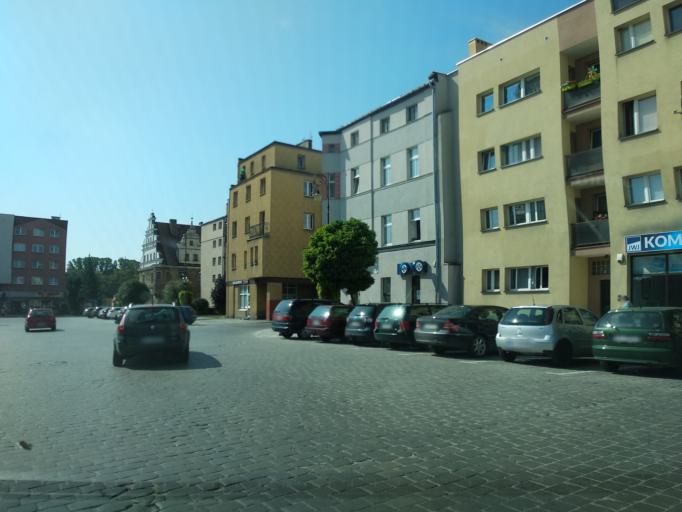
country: PL
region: Lower Silesian Voivodeship
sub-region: Powiat strzelinski
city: Strzelin
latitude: 50.7813
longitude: 17.0706
